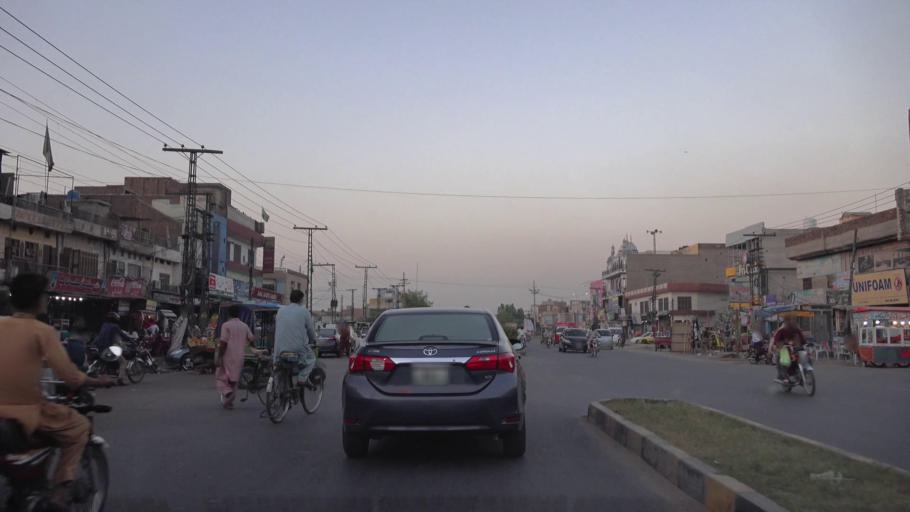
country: PK
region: Punjab
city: Faisalabad
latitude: 31.4509
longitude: 73.0981
